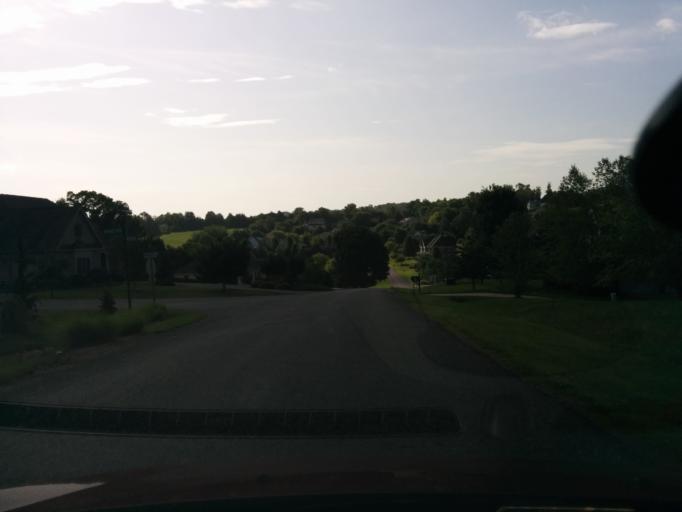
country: US
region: Virginia
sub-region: City of Lexington
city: Lexington
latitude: 37.7685
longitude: -79.4671
